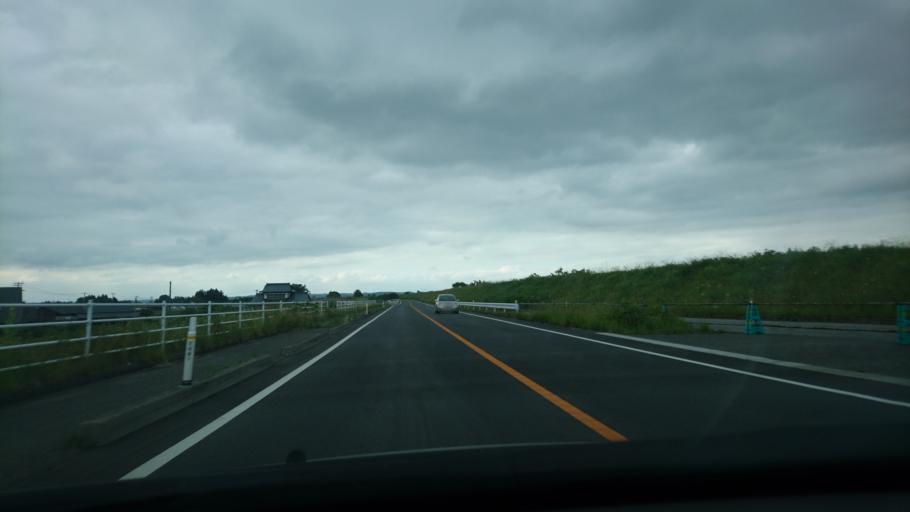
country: JP
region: Iwate
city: Ichinoseki
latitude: 38.7360
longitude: 141.1517
